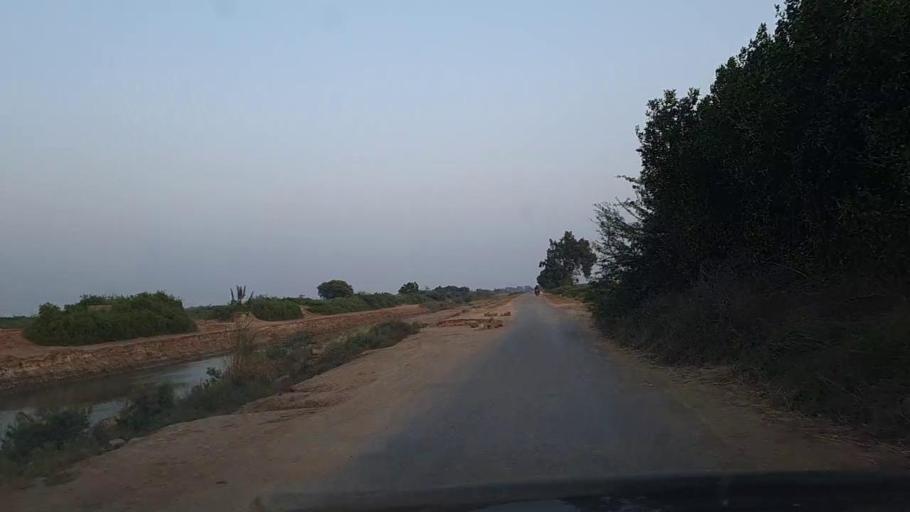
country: PK
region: Sindh
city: Mirpur Sakro
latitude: 24.6312
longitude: 67.6312
